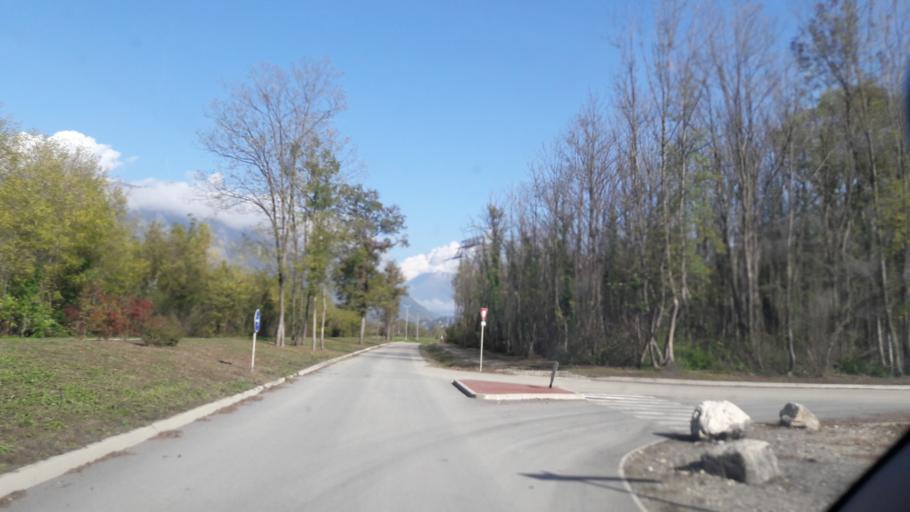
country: FR
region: Rhone-Alpes
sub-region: Departement de l'Isere
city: Chapareillan
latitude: 45.4741
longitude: 6.0221
